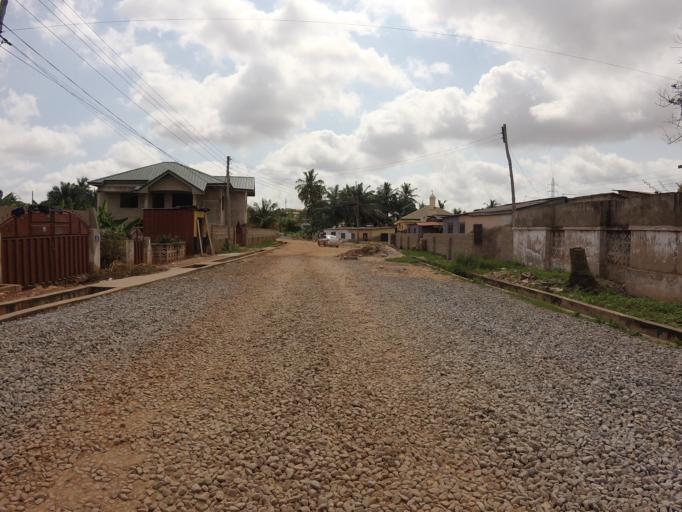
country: GH
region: Greater Accra
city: Dome
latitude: 5.6189
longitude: -0.2445
